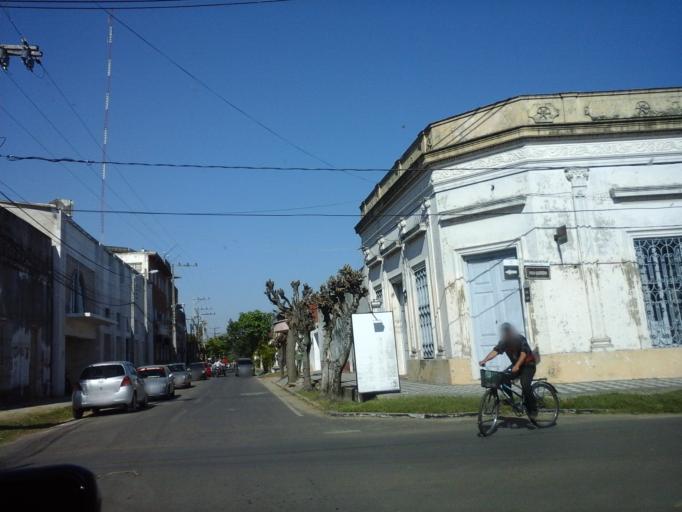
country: PY
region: Neembucu
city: Pilar
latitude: -26.8563
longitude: -58.3076
